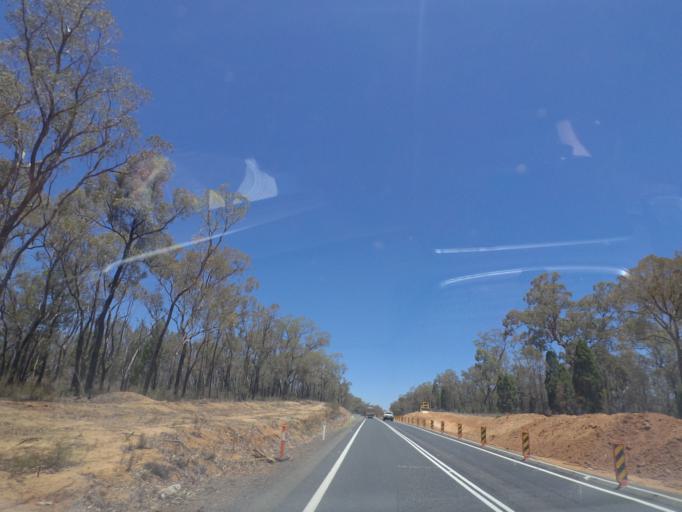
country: AU
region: New South Wales
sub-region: Warrumbungle Shire
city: Coonabarabran
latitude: -30.9226
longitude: 149.4321
